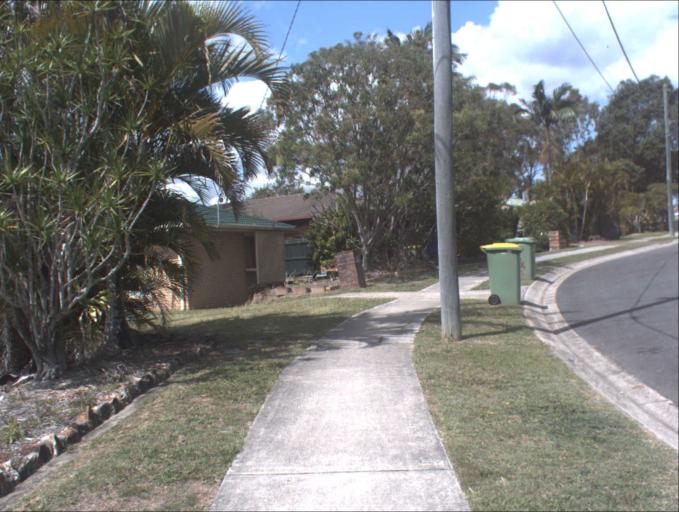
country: AU
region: Queensland
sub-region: Logan
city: Logan City
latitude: -27.6705
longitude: 153.0880
